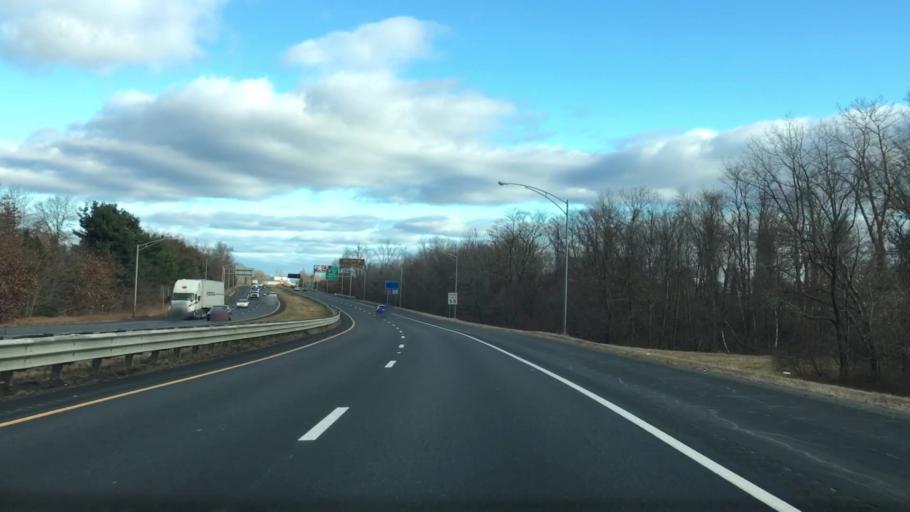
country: US
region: Massachusetts
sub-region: Hampden County
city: Springfield
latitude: 42.1313
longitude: -72.5582
